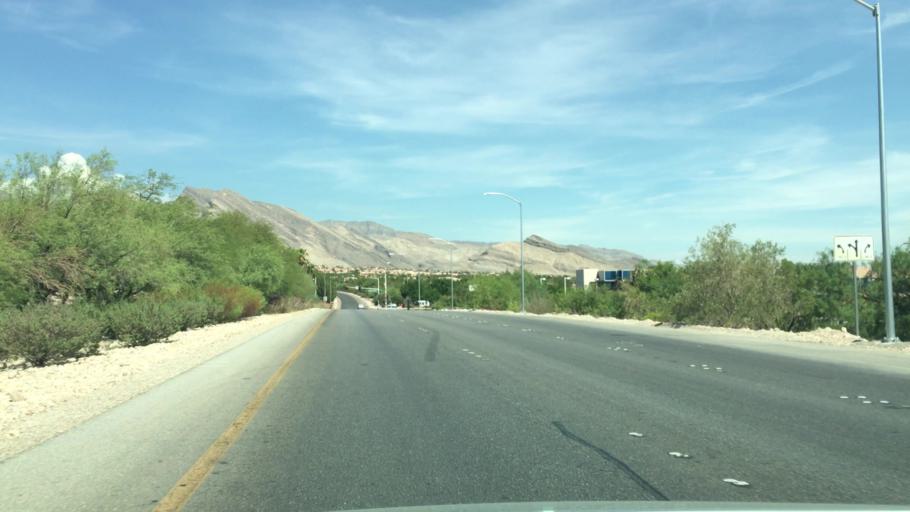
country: US
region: Nevada
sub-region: Clark County
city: Summerlin South
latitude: 36.1857
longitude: -115.3044
